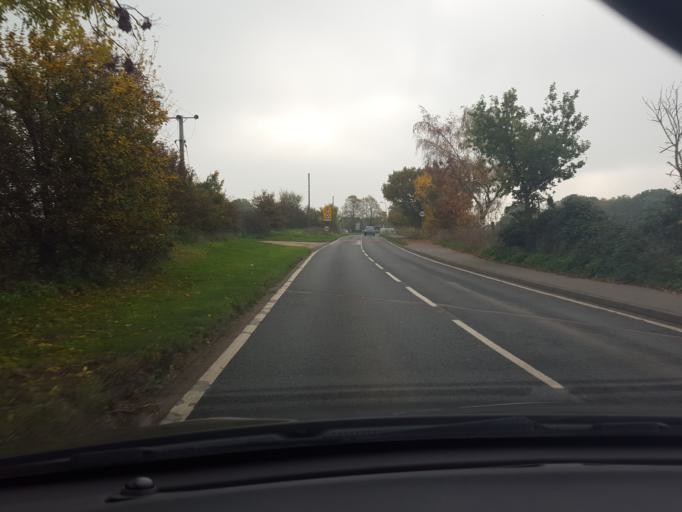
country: GB
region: England
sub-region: Essex
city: Brightlingsea
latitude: 51.8268
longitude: 1.0158
